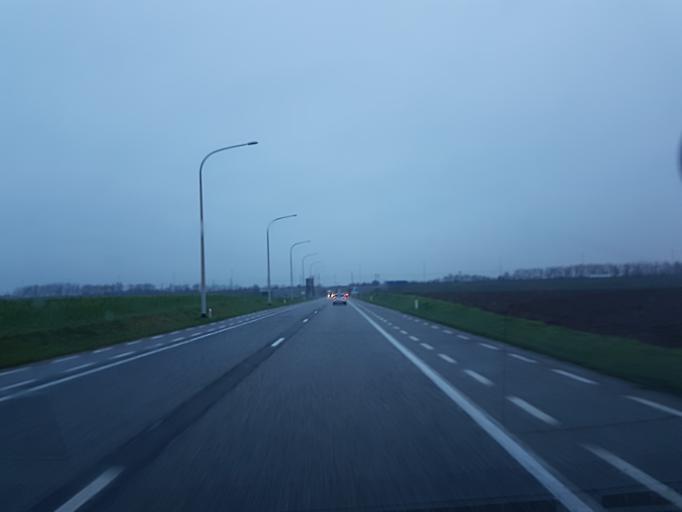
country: BE
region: Wallonia
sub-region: Province de Liege
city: Hannut
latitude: 50.7087
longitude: 5.0817
